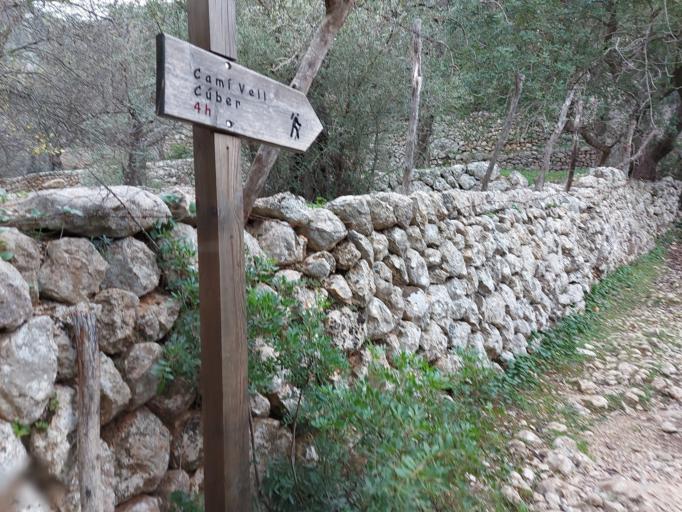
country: ES
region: Balearic Islands
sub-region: Illes Balears
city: Fornalutx
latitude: 39.7675
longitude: 2.7415
